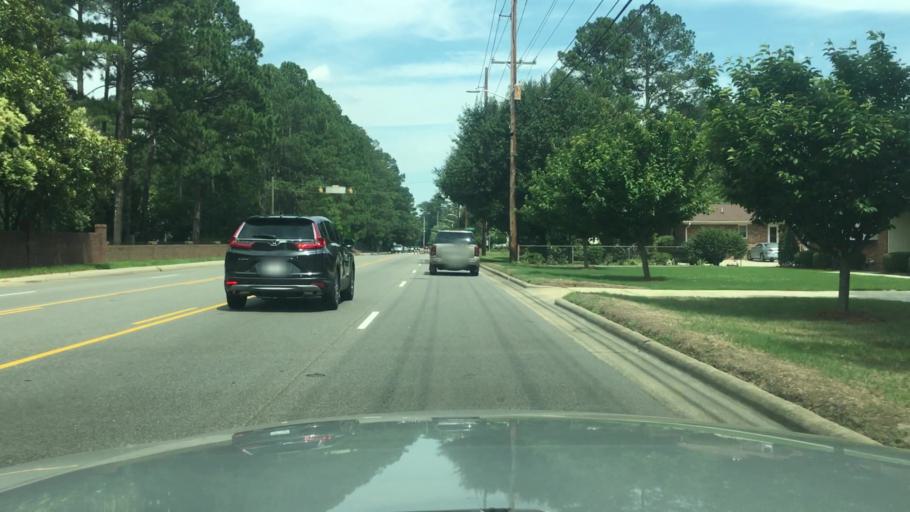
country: US
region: North Carolina
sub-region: Cumberland County
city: Fayetteville
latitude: 35.0649
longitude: -78.9400
